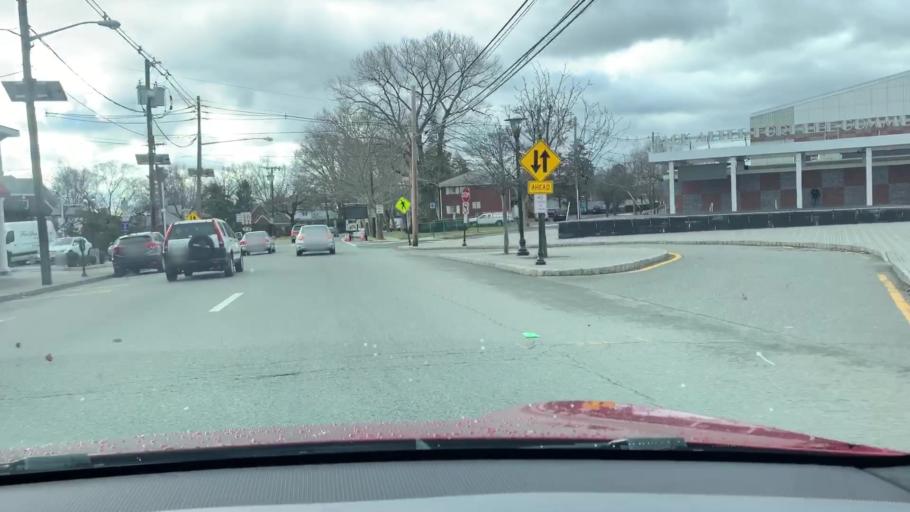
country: US
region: New Jersey
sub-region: Bergen County
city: Fort Lee
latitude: 40.8456
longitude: -73.9788
